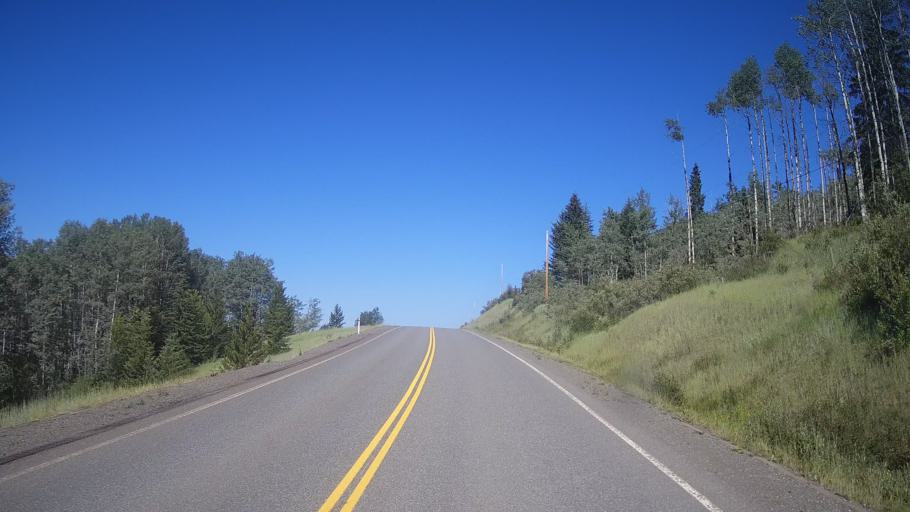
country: CA
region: British Columbia
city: Kamloops
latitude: 51.4960
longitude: -120.5786
